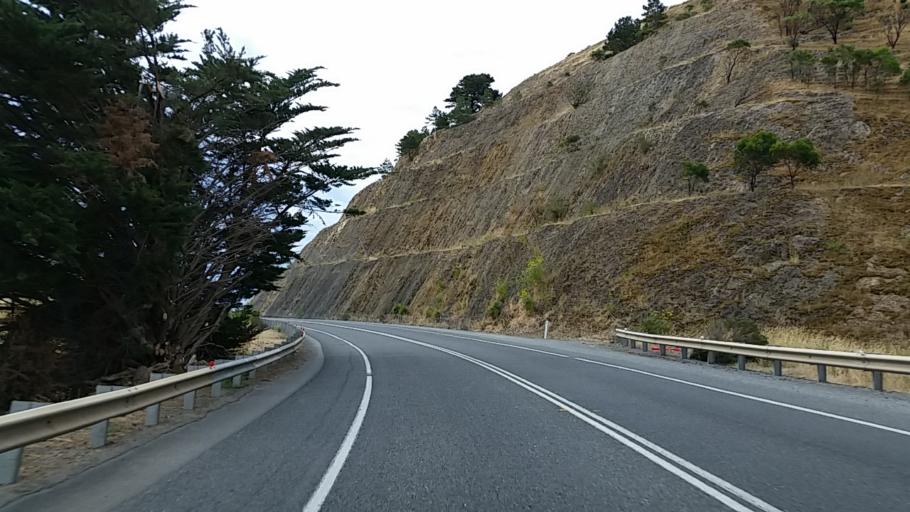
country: AU
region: South Australia
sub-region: Onkaparinga
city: Aldinga
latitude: -35.3640
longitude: 138.4558
